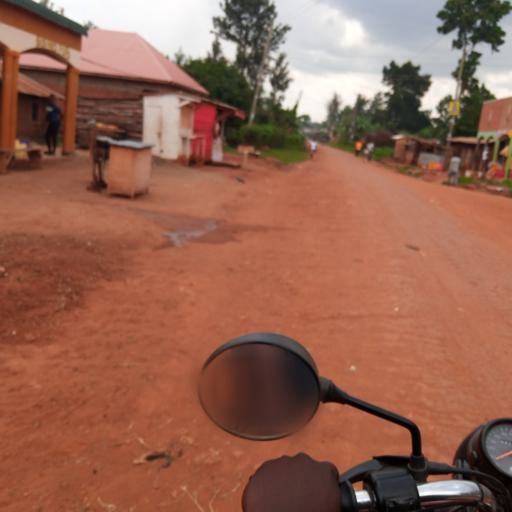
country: UG
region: Eastern Region
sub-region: Mbale District
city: Mbale
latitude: 1.1075
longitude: 34.1765
